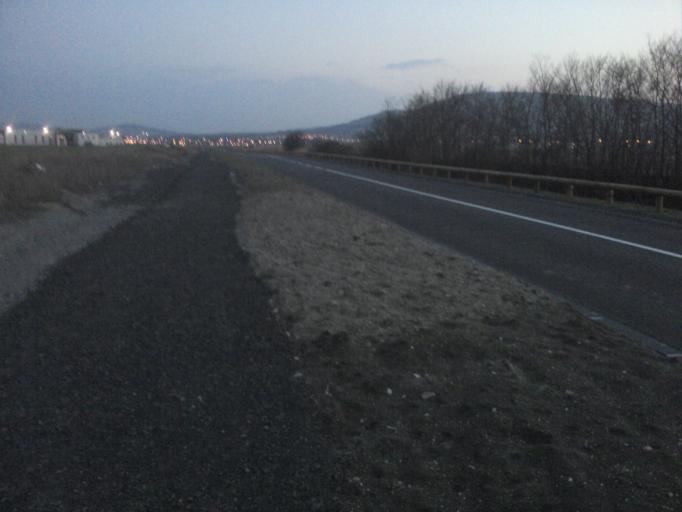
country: FR
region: Auvergne
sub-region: Departement du Puy-de-Dome
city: Perignat-les-Sarlieve
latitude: 45.7536
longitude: 3.1508
